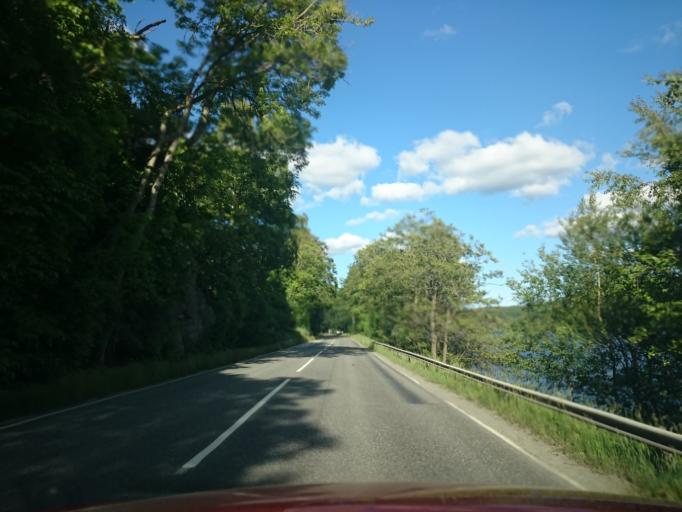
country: SE
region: Vaestra Goetaland
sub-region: Harryda Kommun
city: Molnlycke
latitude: 57.6752
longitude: 12.1536
